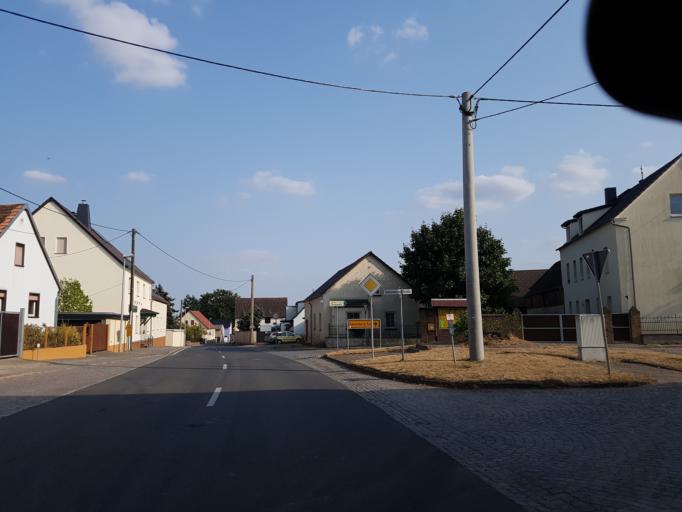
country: DE
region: Saxony
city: Dommitzsch
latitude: 51.6619
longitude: 12.8532
